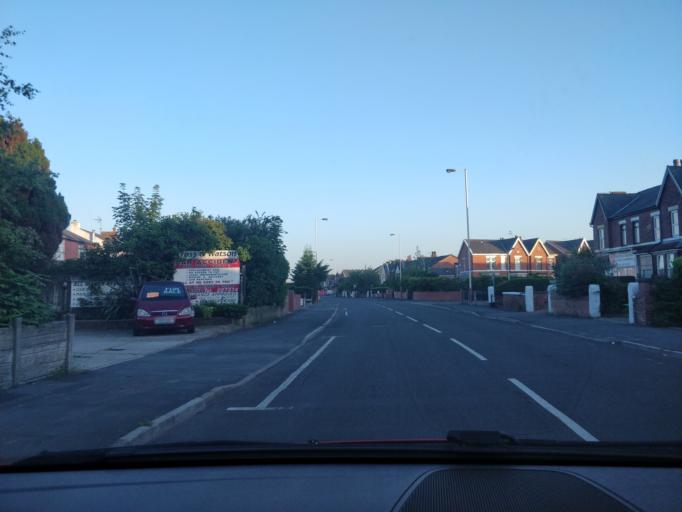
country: GB
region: England
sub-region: Sefton
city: Southport
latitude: 53.6519
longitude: -2.9674
